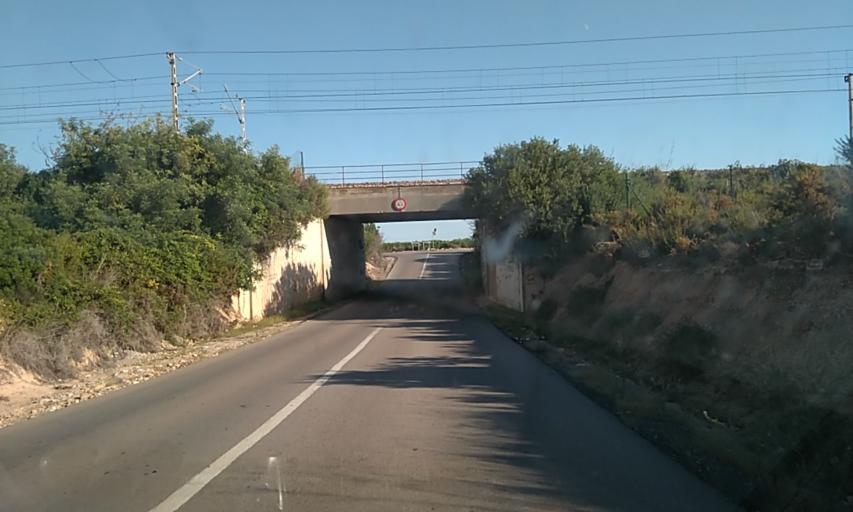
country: ES
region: Valencia
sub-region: Provincia de Castello
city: Torreblanca
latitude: 40.2455
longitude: 0.2330
